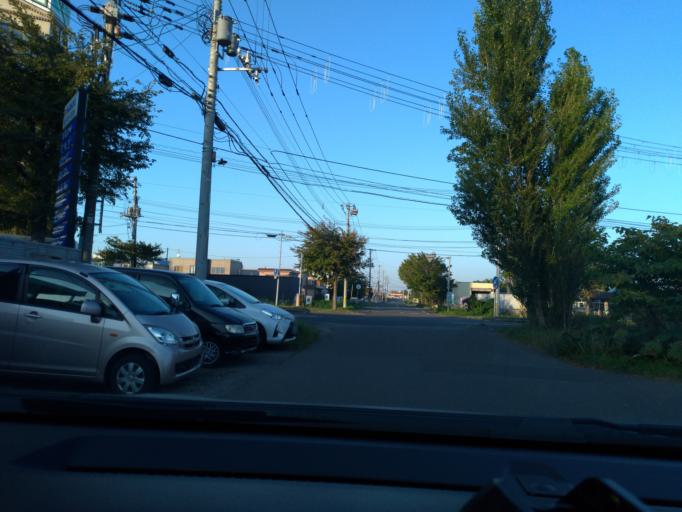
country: JP
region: Hokkaido
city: Ishikari
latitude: 43.1585
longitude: 141.3536
